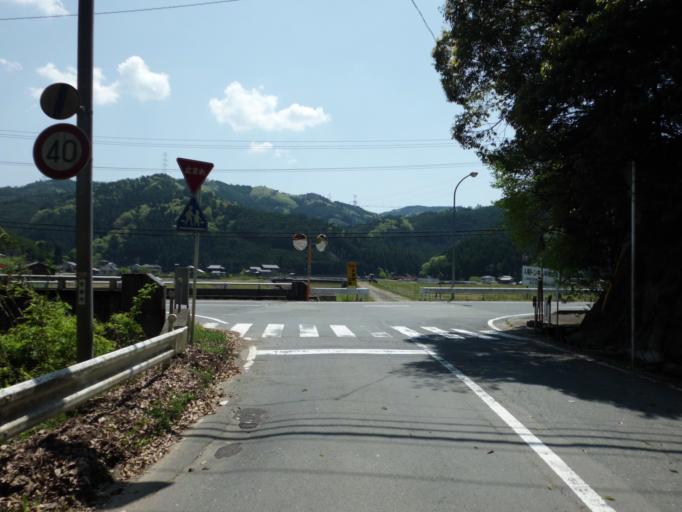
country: JP
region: Kyoto
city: Kameoka
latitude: 35.1441
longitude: 135.5900
